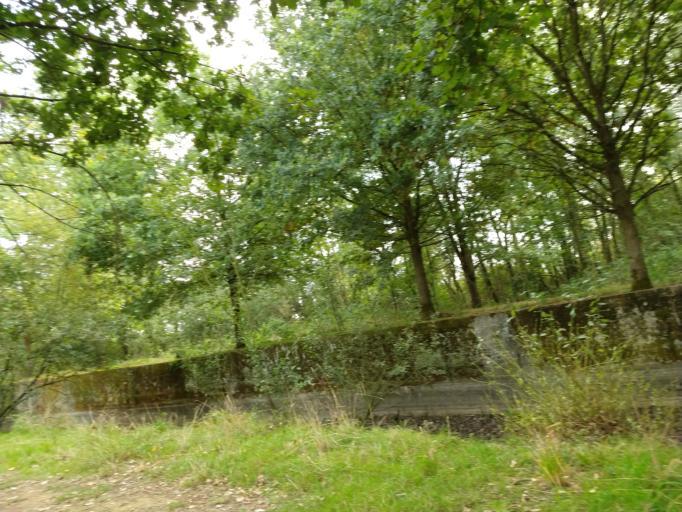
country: BE
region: Flanders
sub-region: Provincie Vlaams-Brabant
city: Haacht
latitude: 50.9805
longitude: 4.6561
